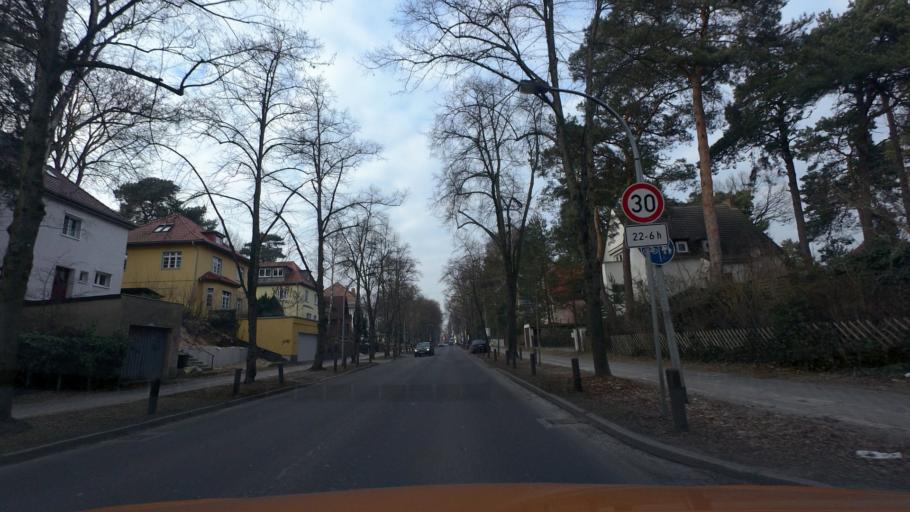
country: DE
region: Brandenburg
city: Kleinmachnow
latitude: 52.4034
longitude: 13.2374
